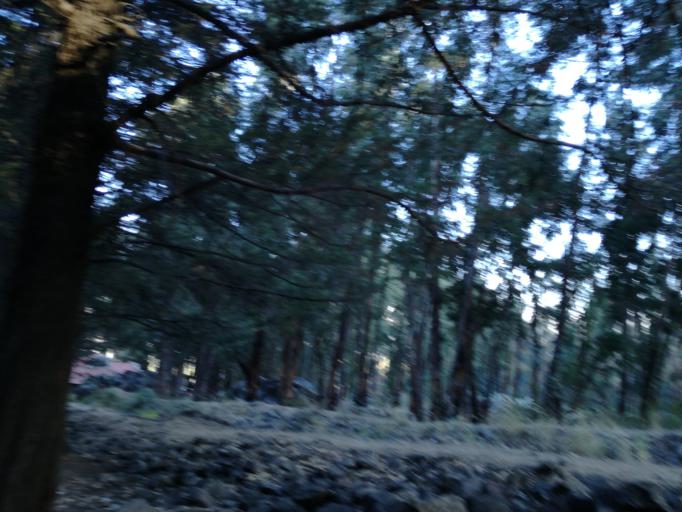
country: BO
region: Cochabamba
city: Sipe Sipe
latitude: -17.3431
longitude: -66.3323
